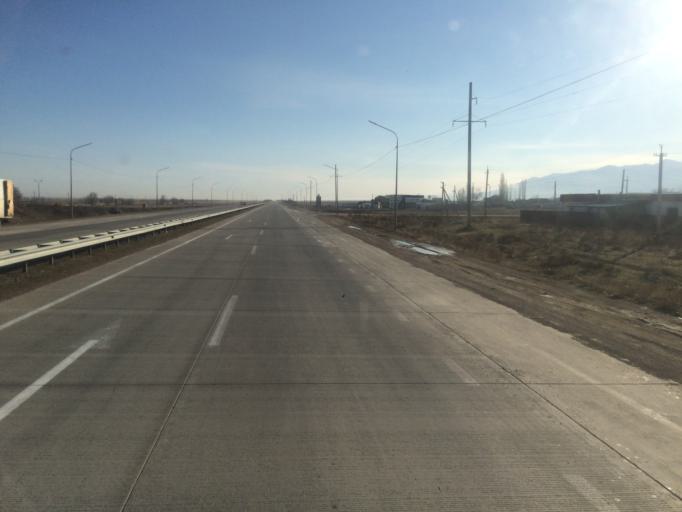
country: KZ
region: Zhambyl
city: Sarykemer
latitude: 43.0088
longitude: 71.8036
